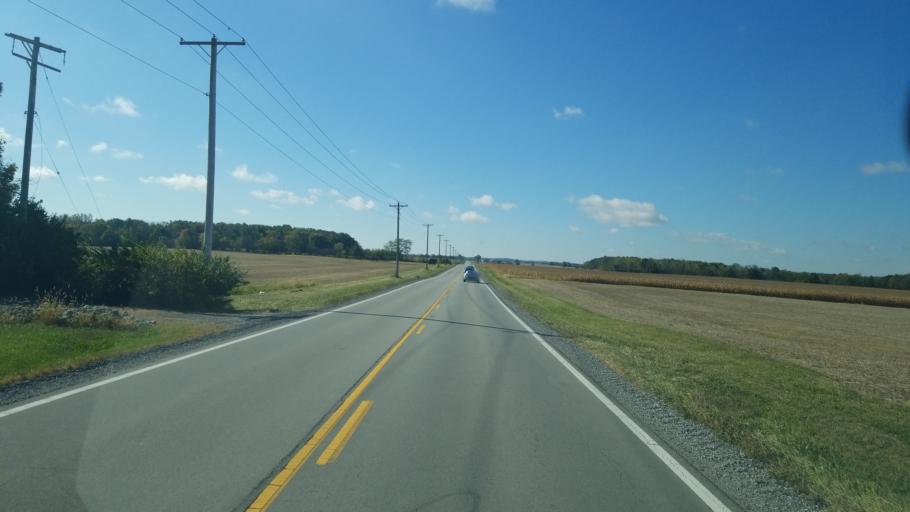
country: US
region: Ohio
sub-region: Highland County
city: Leesburg
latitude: 39.4229
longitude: -83.5185
